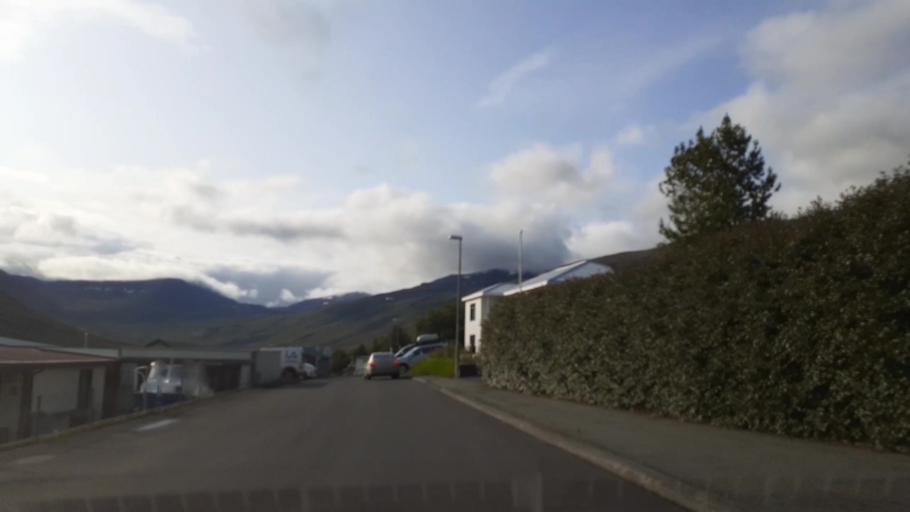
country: IS
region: East
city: Eskifjoerdur
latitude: 65.0657
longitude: -14.0000
